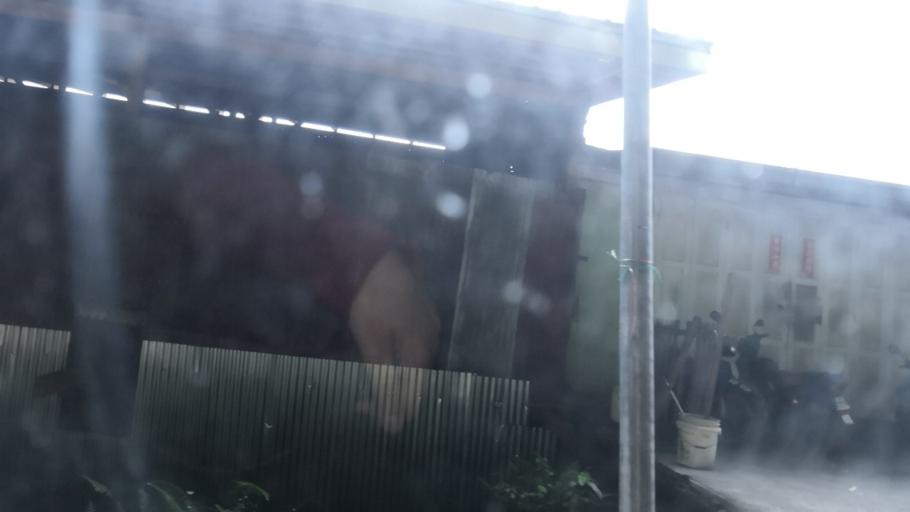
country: MY
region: Perak
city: Lumut
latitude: 4.2160
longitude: 100.5764
